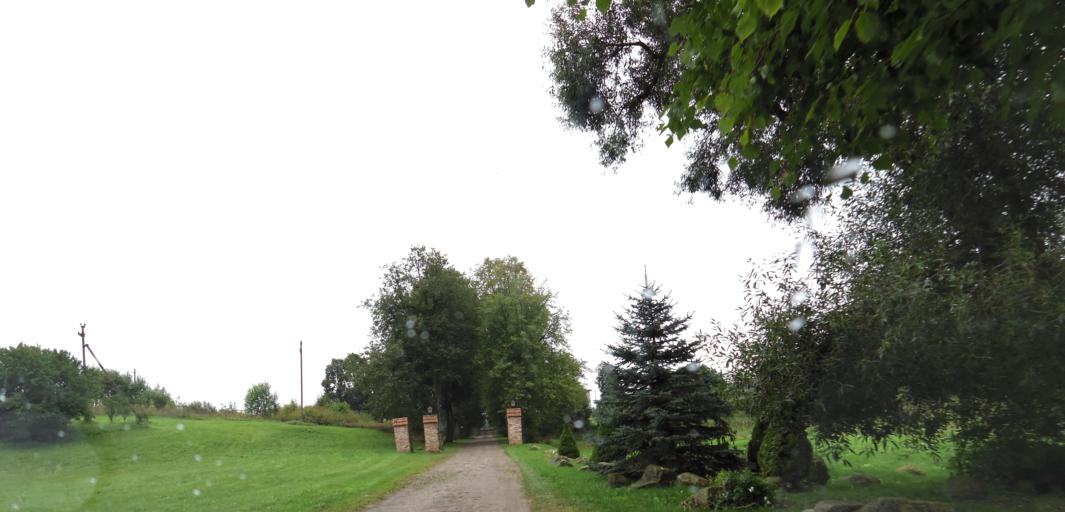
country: LT
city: Sirvintos
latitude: 55.0762
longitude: 25.0615
